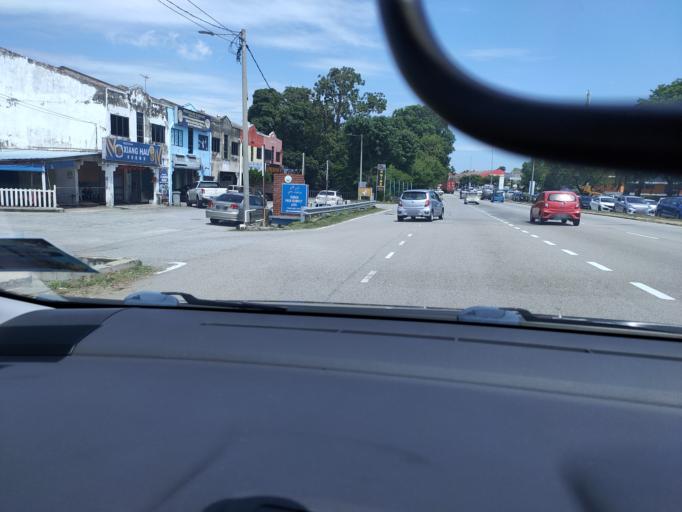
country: MY
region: Melaka
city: Bukit Rambai
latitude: 2.2801
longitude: 102.2152
